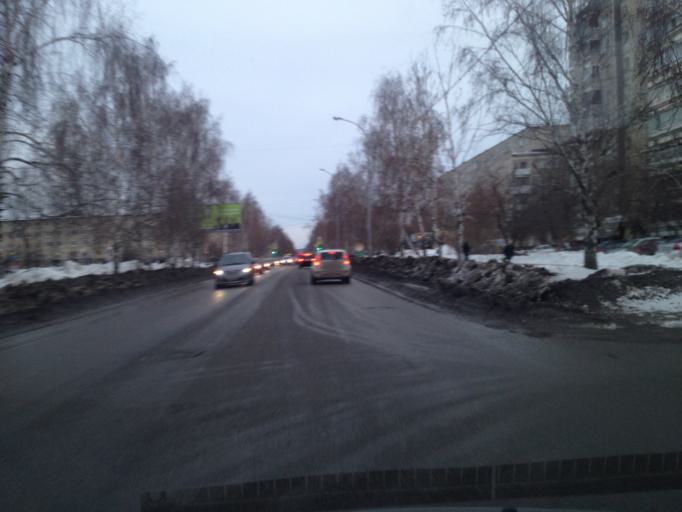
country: RU
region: Sverdlovsk
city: Sovkhoznyy
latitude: 56.8088
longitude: 60.5497
